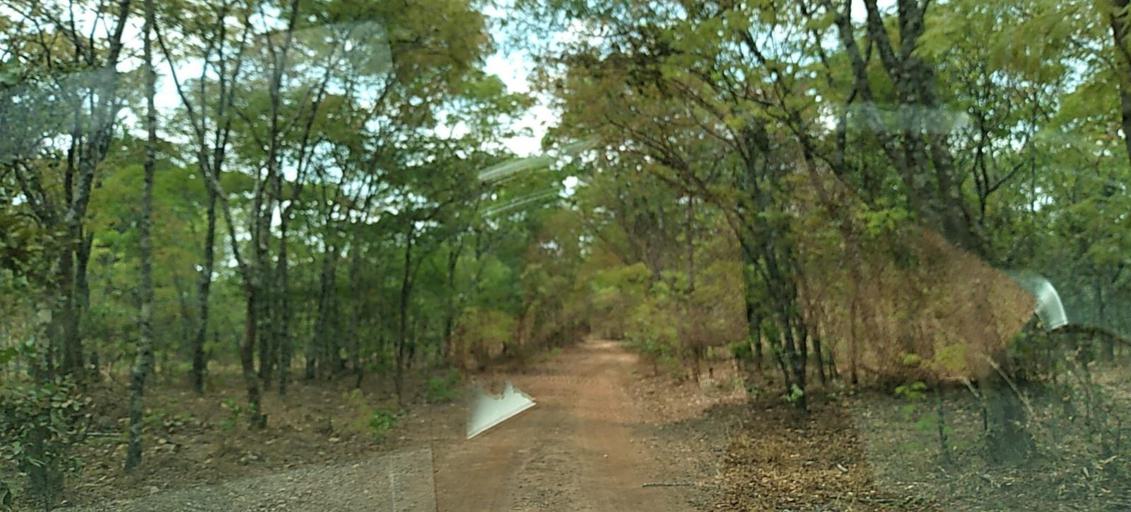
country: ZM
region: Copperbelt
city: Chililabombwe
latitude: -12.5024
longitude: 27.6376
